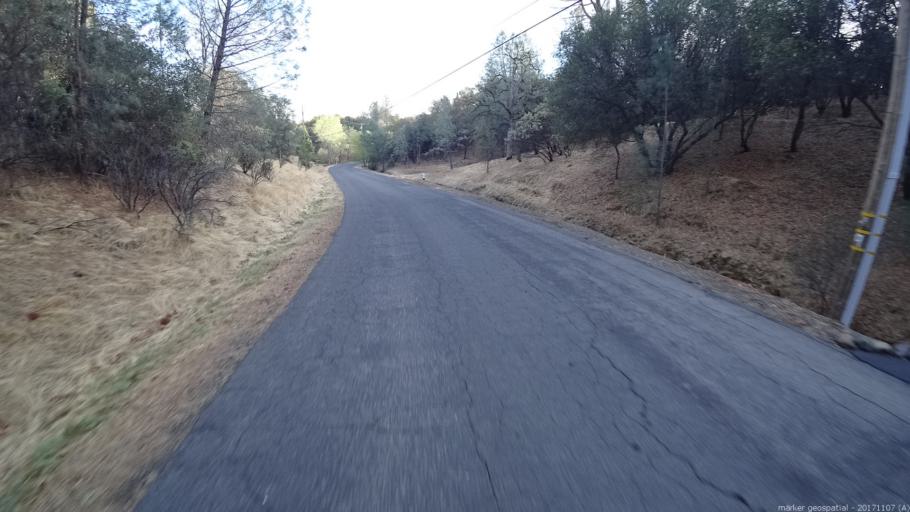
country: US
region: California
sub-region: Shasta County
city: Shasta
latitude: 40.5374
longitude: -122.4846
